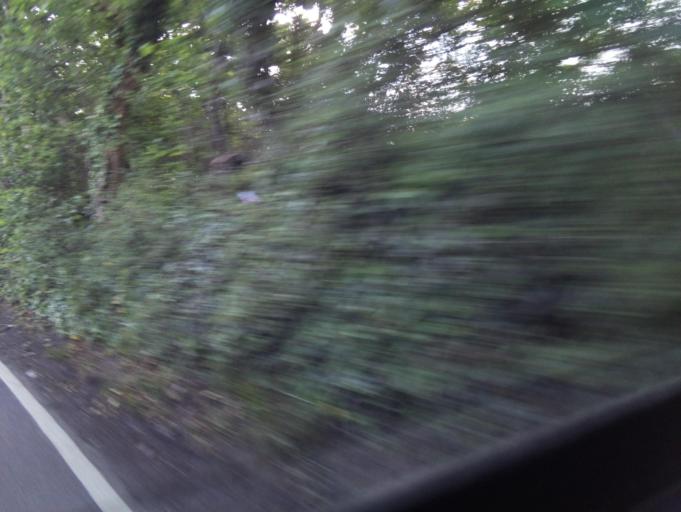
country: GB
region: England
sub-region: Hertfordshire
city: Chorleywood
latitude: 51.6724
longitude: -0.4615
